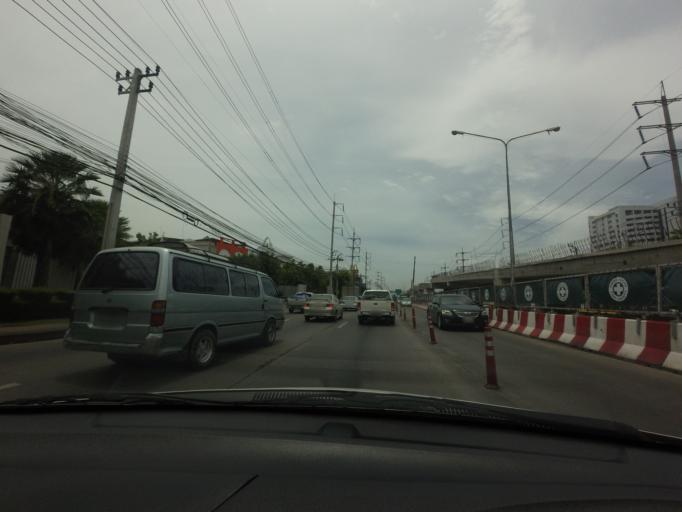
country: TH
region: Bangkok
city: Khan Na Yao
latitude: 13.8136
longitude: 100.6887
